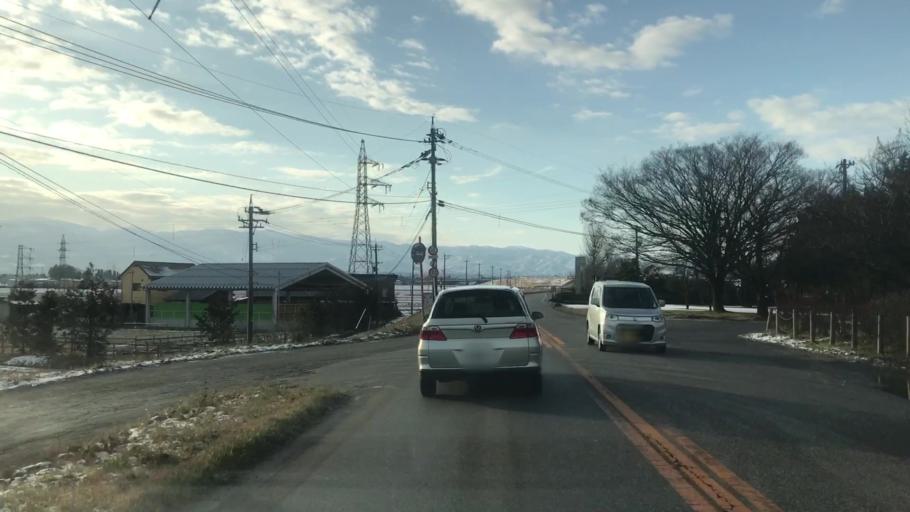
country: JP
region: Toyama
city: Toyama-shi
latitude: 36.6852
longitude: 137.2844
